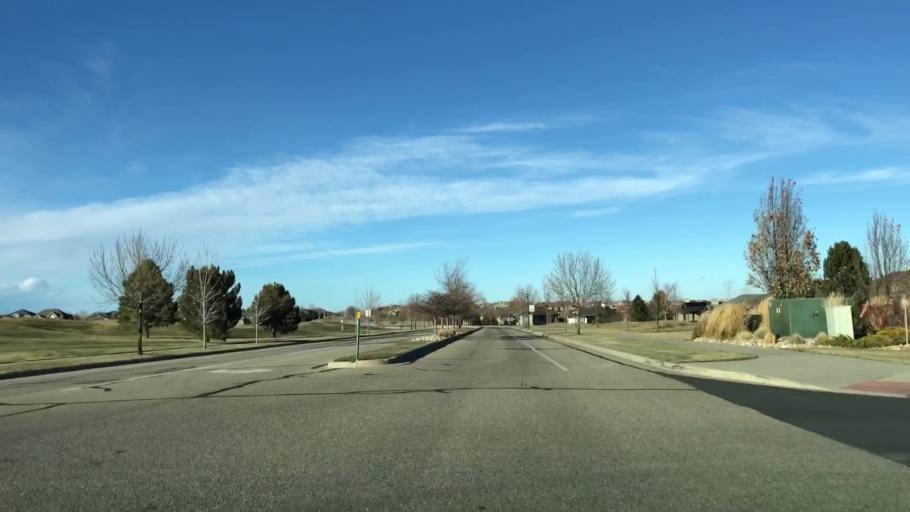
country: US
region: Colorado
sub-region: Weld County
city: Windsor
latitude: 40.4578
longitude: -104.9767
